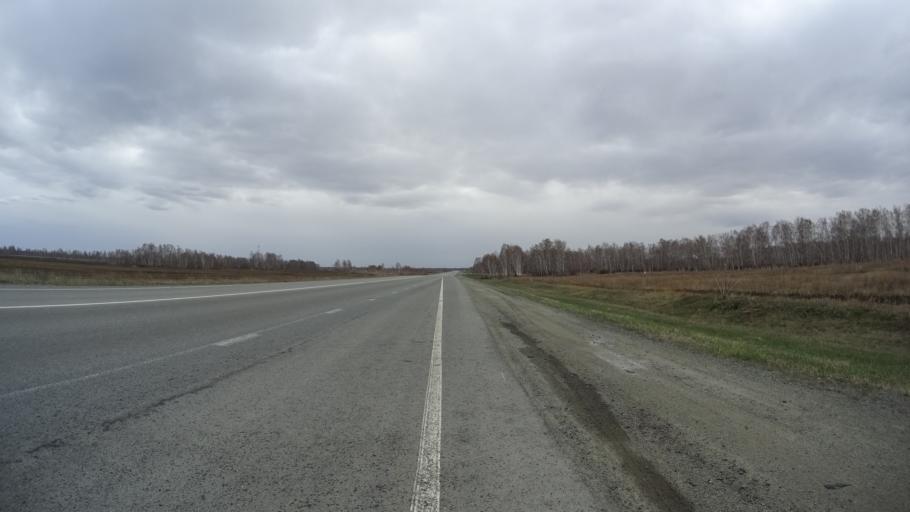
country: RU
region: Chelyabinsk
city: Yemanzhelinsk
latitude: 54.6951
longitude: 61.2496
